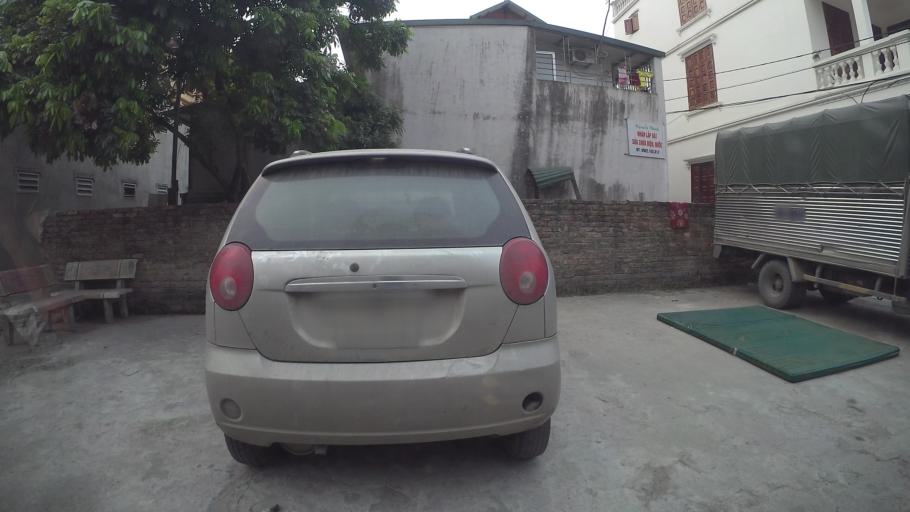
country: VN
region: Ha Noi
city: Hoan Kiem
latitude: 21.0719
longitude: 105.8881
